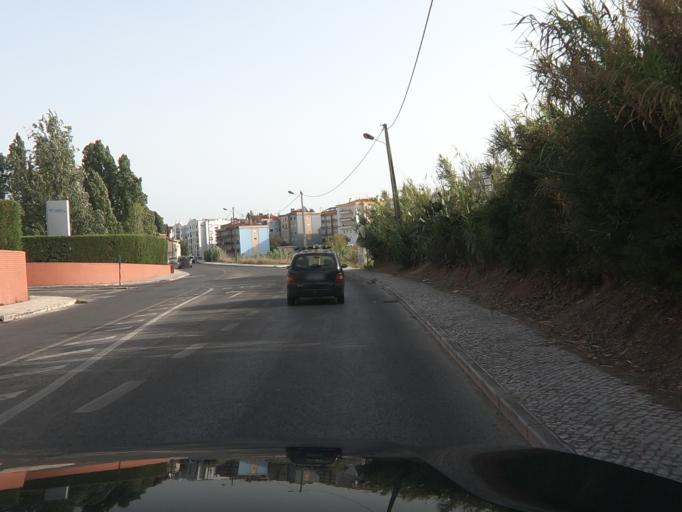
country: PT
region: Setubal
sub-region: Setubal
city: Setubal
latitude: 38.5377
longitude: -8.8984
